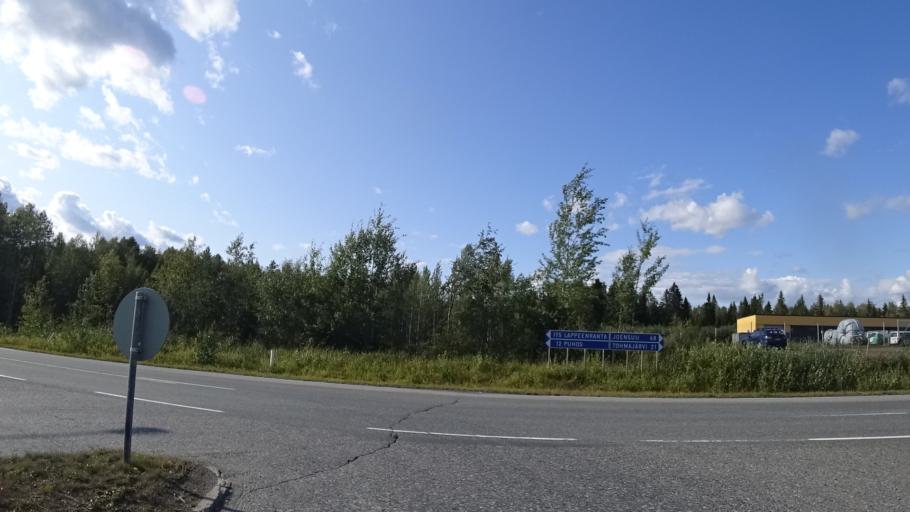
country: FI
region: North Karelia
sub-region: Keski-Karjala
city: Kitee
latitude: 62.0976
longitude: 30.1108
